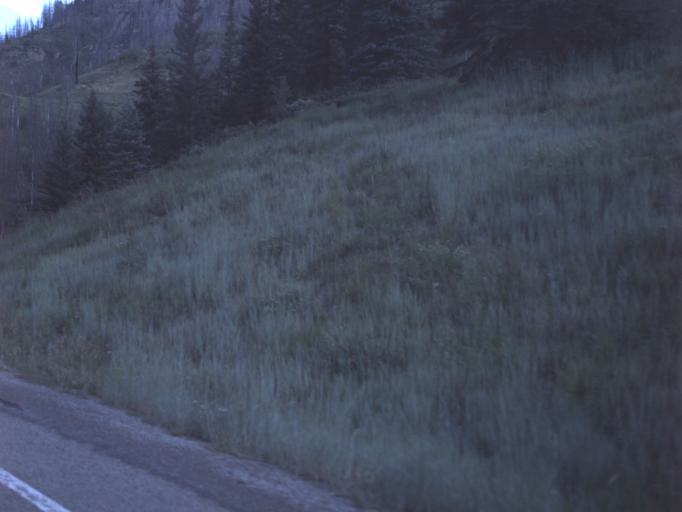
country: US
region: Utah
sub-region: Sanpete County
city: Fairview
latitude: 39.5458
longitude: -111.1648
